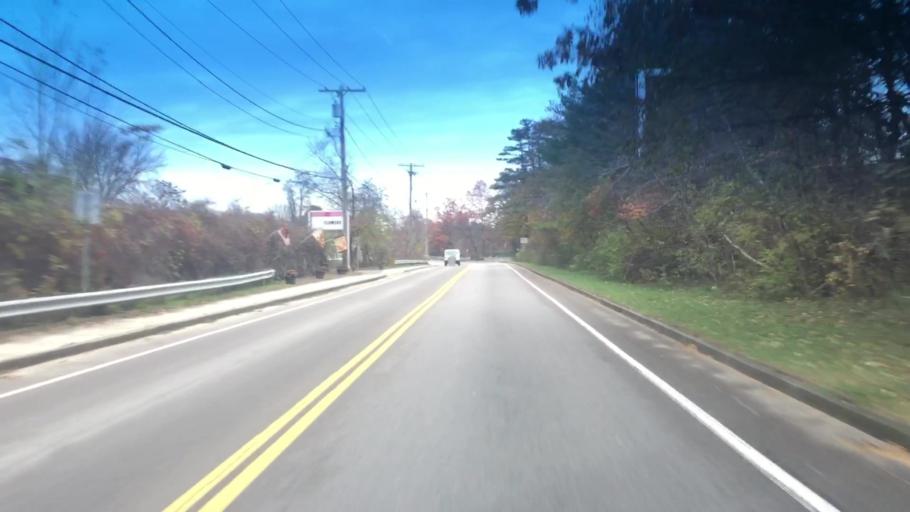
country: US
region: Massachusetts
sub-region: Norfolk County
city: Medfield
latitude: 42.1794
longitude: -71.3266
